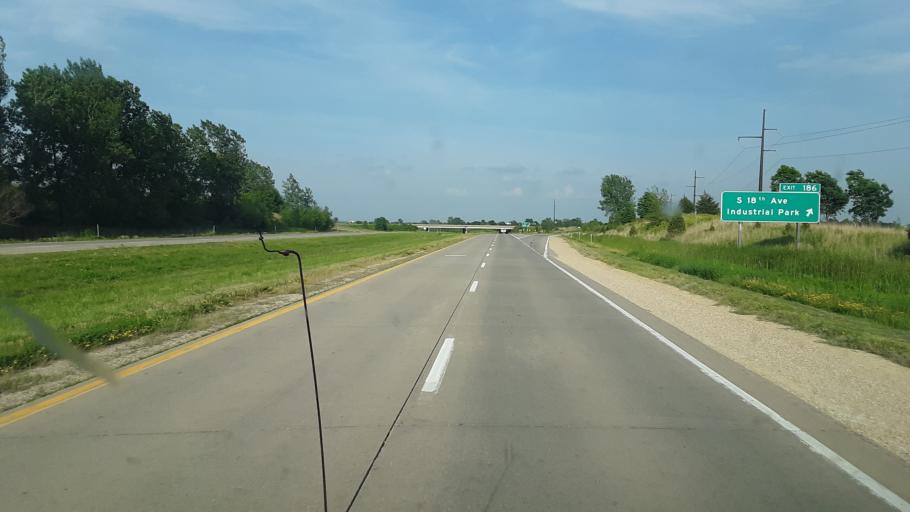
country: US
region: Iowa
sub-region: Marshall County
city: Marshalltown
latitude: 42.0030
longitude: -92.8907
